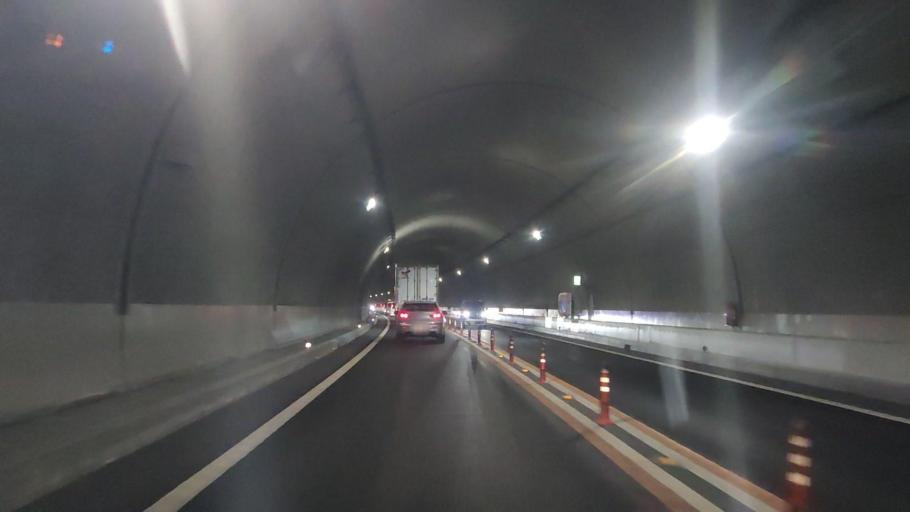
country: JP
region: Fukuoka
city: Kanda
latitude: 33.7861
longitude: 130.9715
